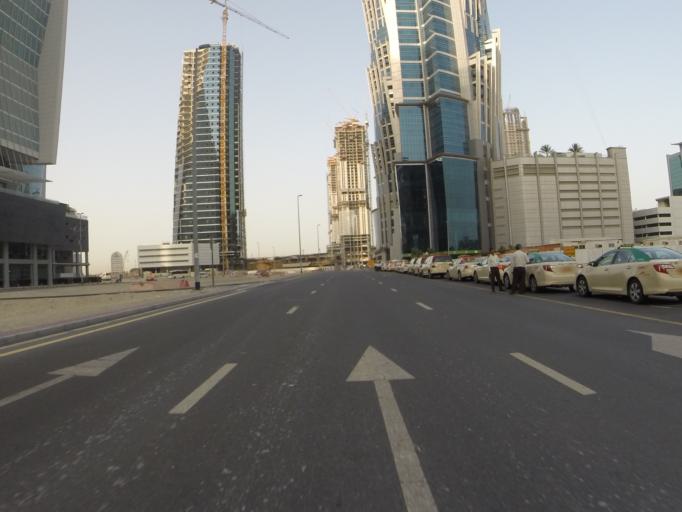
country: AE
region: Dubai
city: Dubai
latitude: 25.1869
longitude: 55.2597
